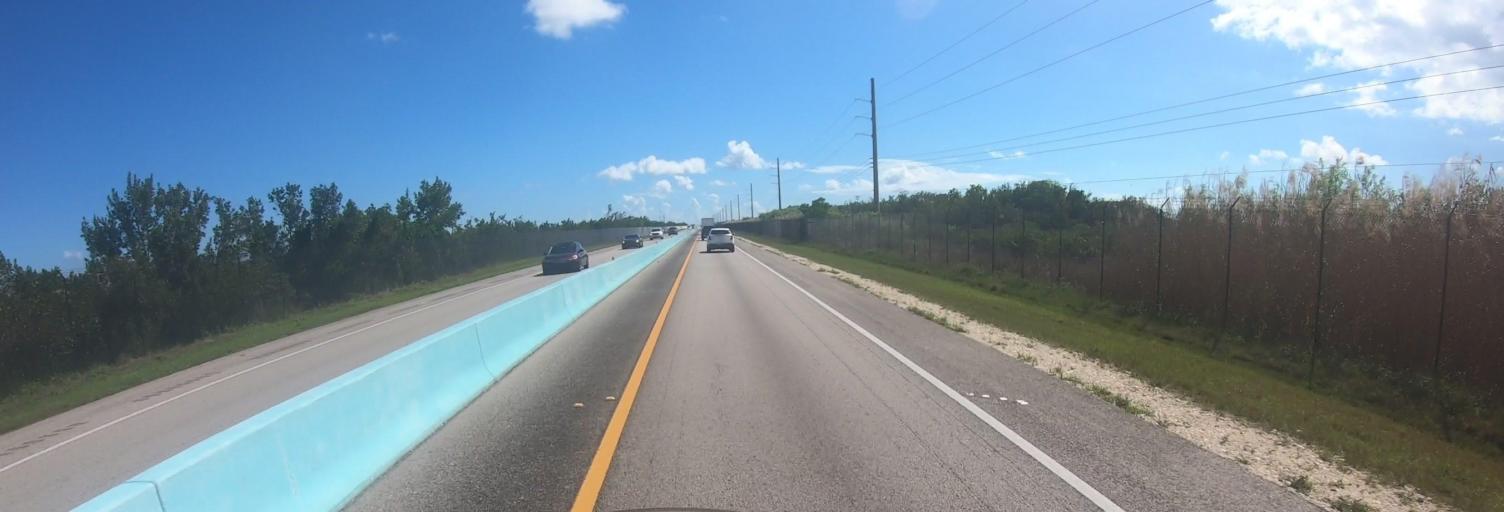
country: US
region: Florida
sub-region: Monroe County
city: North Key Largo
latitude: 25.3053
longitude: -80.4483
